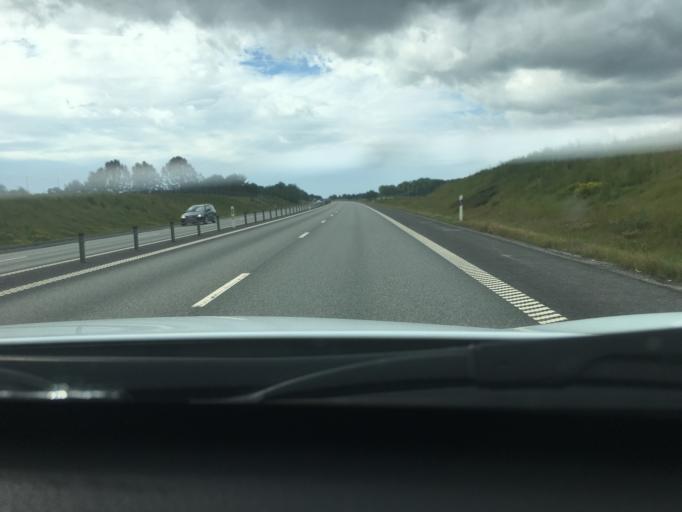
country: SE
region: Blekinge
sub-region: Karlshamns Kommun
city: Morrum
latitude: 56.1556
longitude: 14.6656
